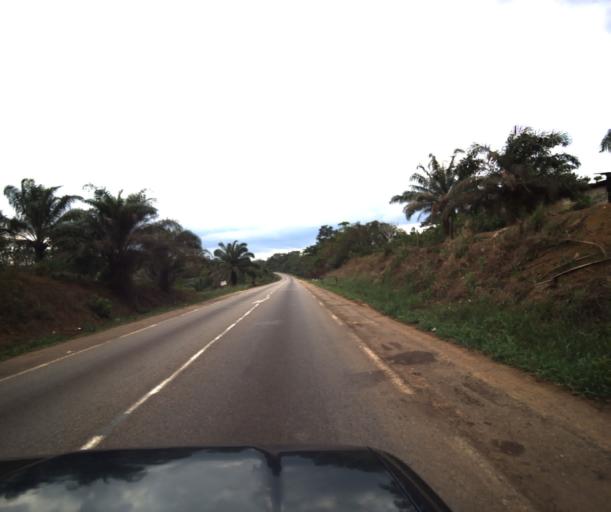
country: CM
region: Littoral
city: Edea
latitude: 3.9412
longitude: 10.0471
